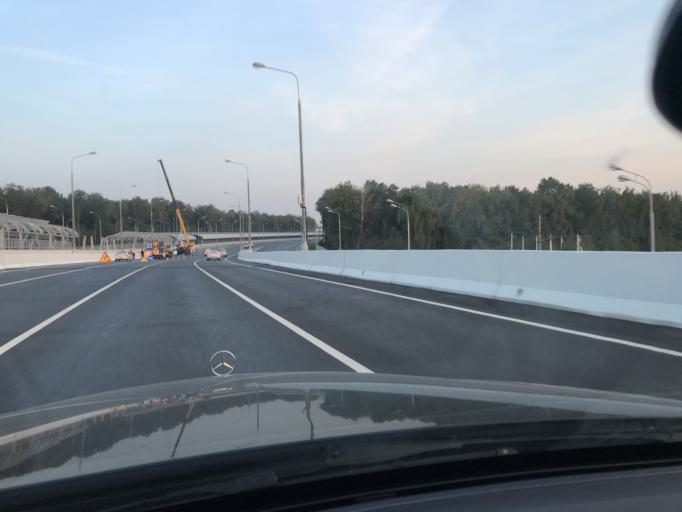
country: RU
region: Moskovskaya
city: Mosrentgen
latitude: 55.5829
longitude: 37.4419
